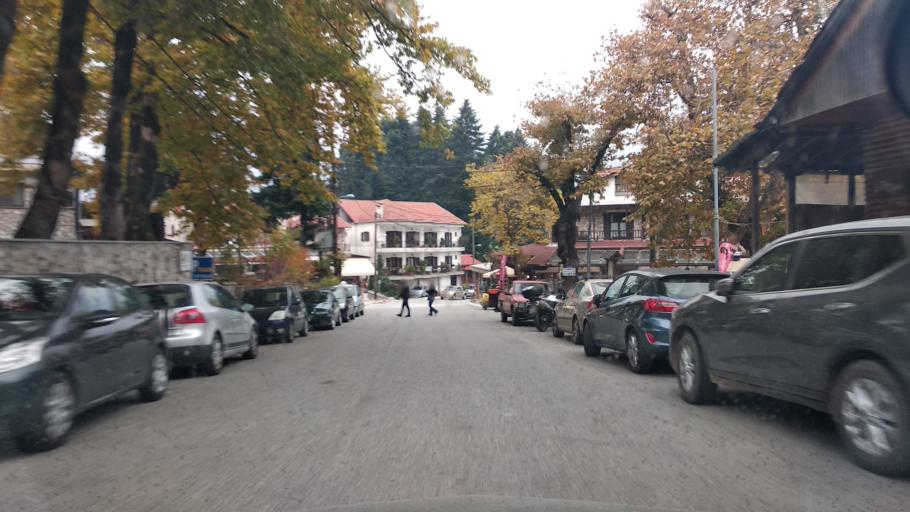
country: GR
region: Thessaly
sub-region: Trikala
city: Pyli
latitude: 39.5012
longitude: 21.5395
